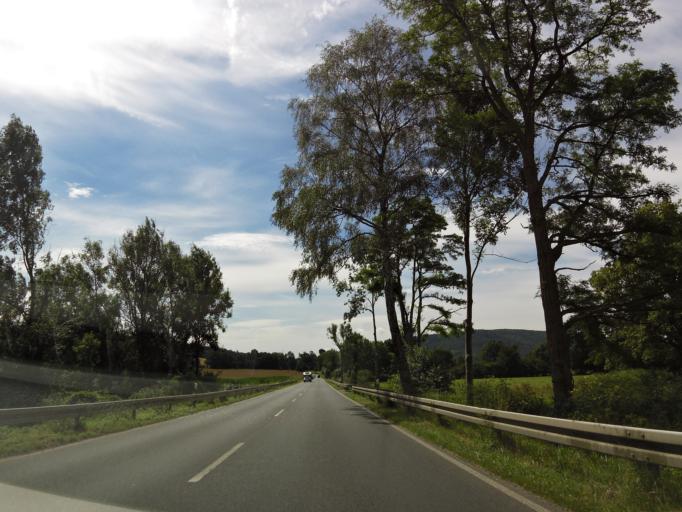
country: DE
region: Lower Saxony
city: Boffzen
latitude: 51.7295
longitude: 9.3698
